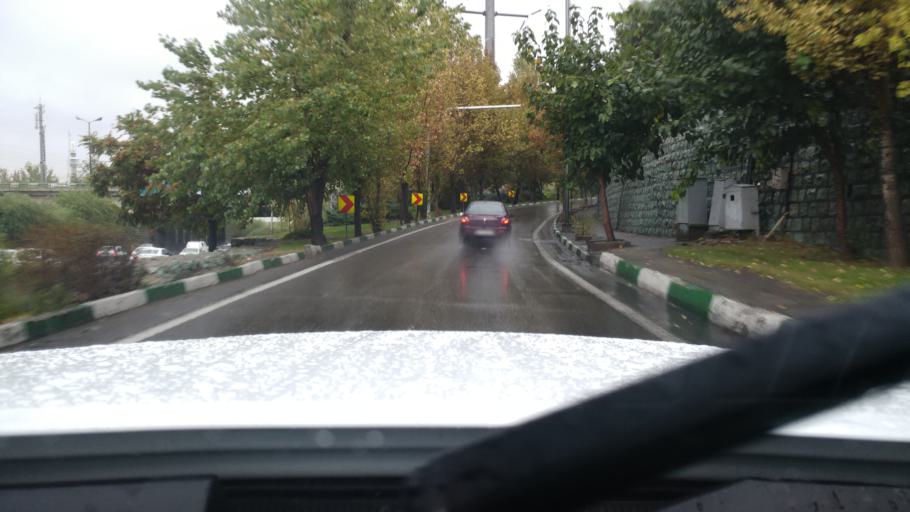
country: IR
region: Tehran
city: Tehran
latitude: 35.7389
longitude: 51.4161
